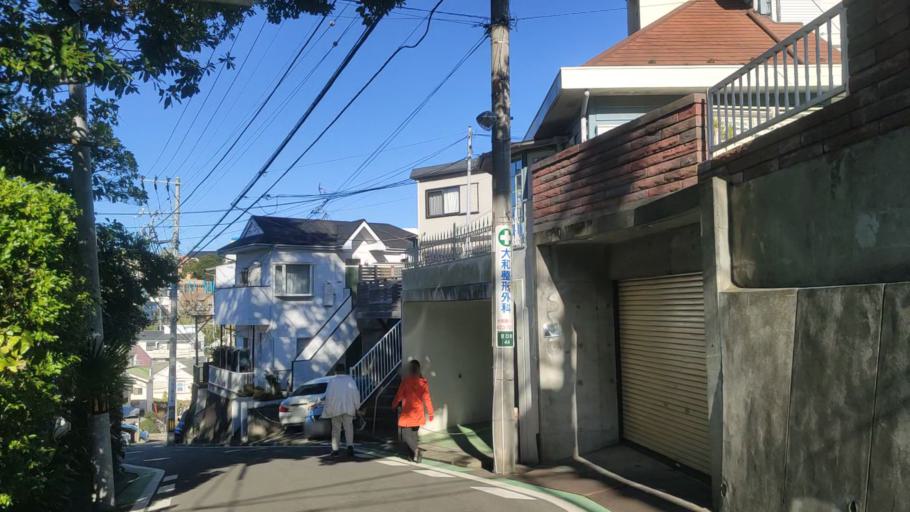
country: JP
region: Kanagawa
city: Yokohama
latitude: 35.4236
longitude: 139.6456
